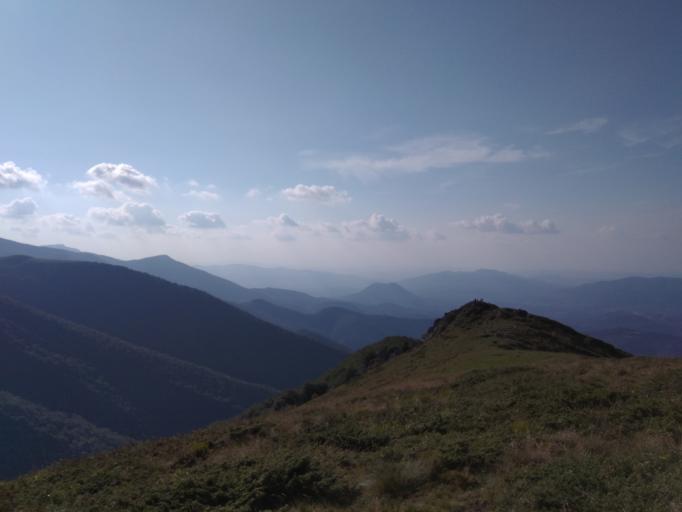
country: BG
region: Stara Zagora
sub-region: Obshtina Pavel Banya
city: Asen
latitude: 42.7608
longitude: 25.1026
